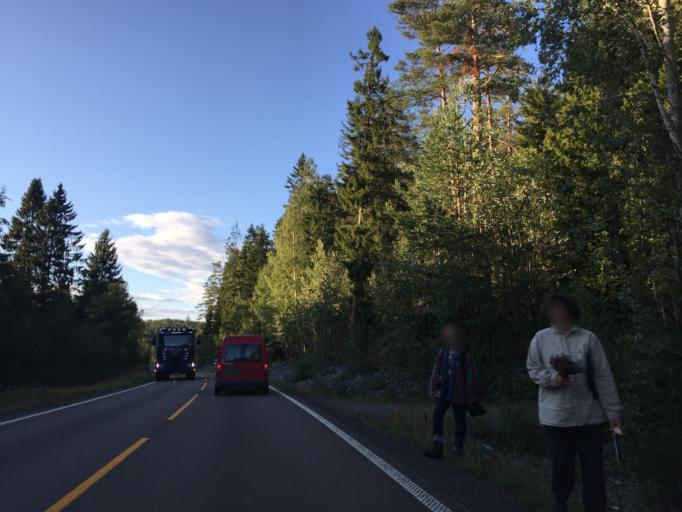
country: NO
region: Akershus
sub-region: Enebakk
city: Flateby
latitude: 59.8228
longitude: 11.2436
